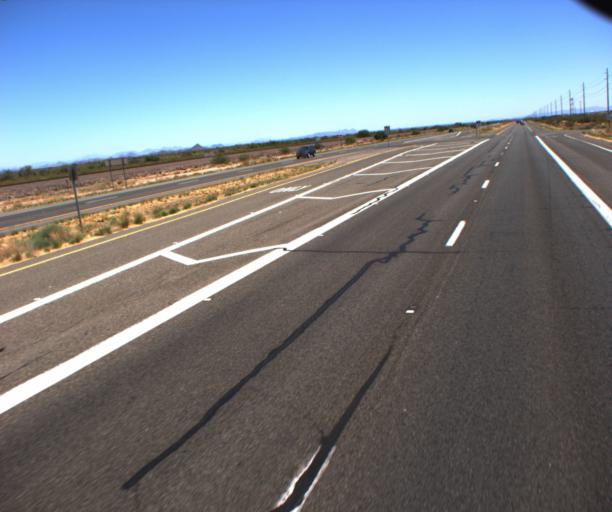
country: US
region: Arizona
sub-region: Maricopa County
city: Sun City West
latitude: 33.7538
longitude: -112.4980
